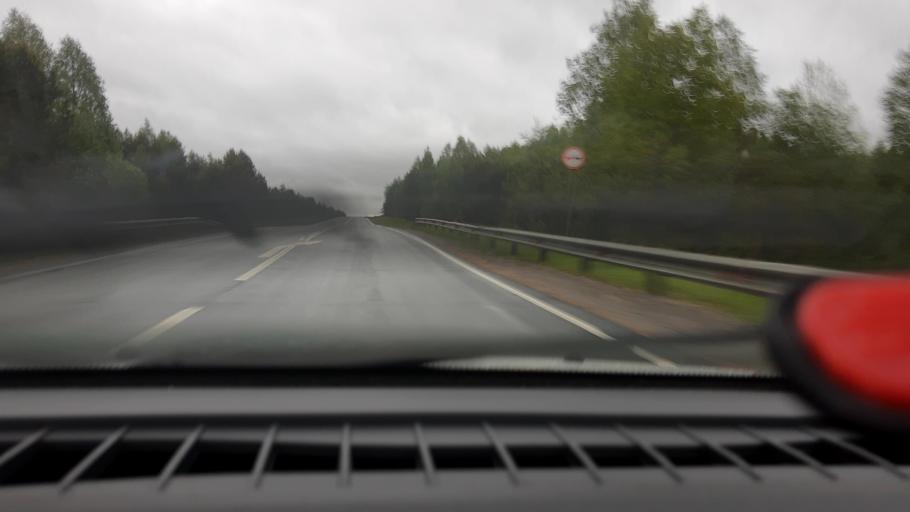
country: RU
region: Nizjnij Novgorod
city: Vladimirskoye
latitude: 56.9756
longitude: 45.1136
